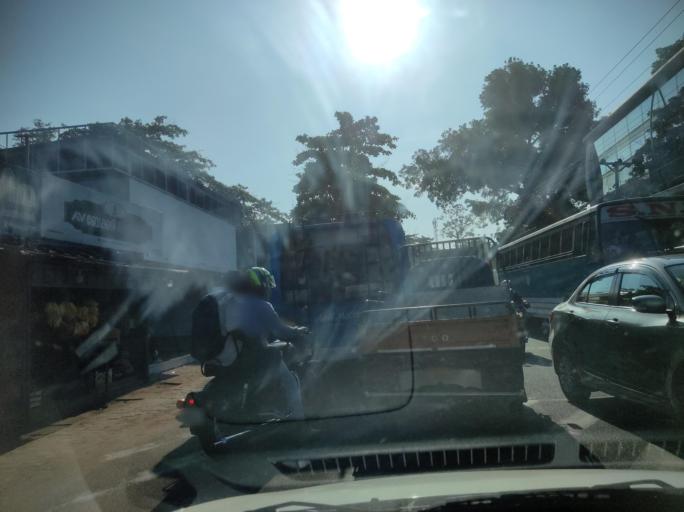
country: IN
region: Kerala
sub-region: Alappuzha
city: Kattanam
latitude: 9.1748
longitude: 76.6413
